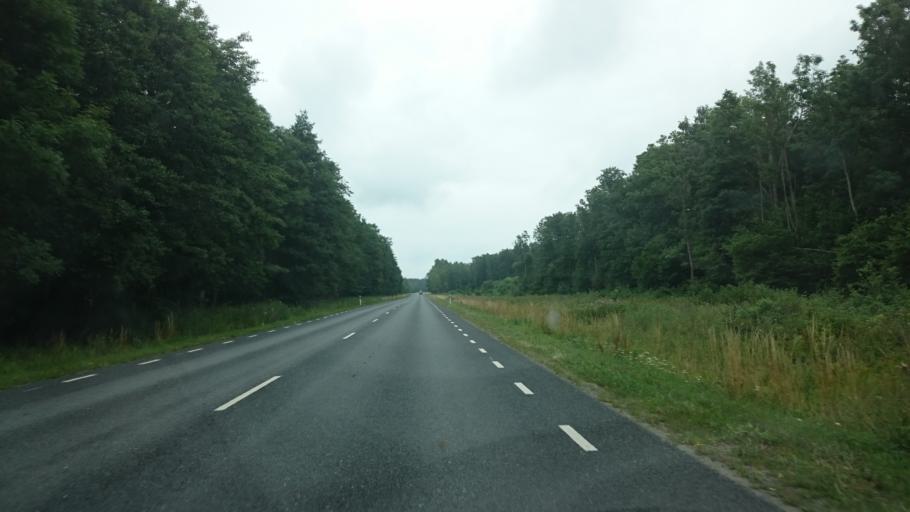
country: EE
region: Saare
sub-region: Orissaare vald
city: Orissaare
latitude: 58.6043
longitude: 23.3021
